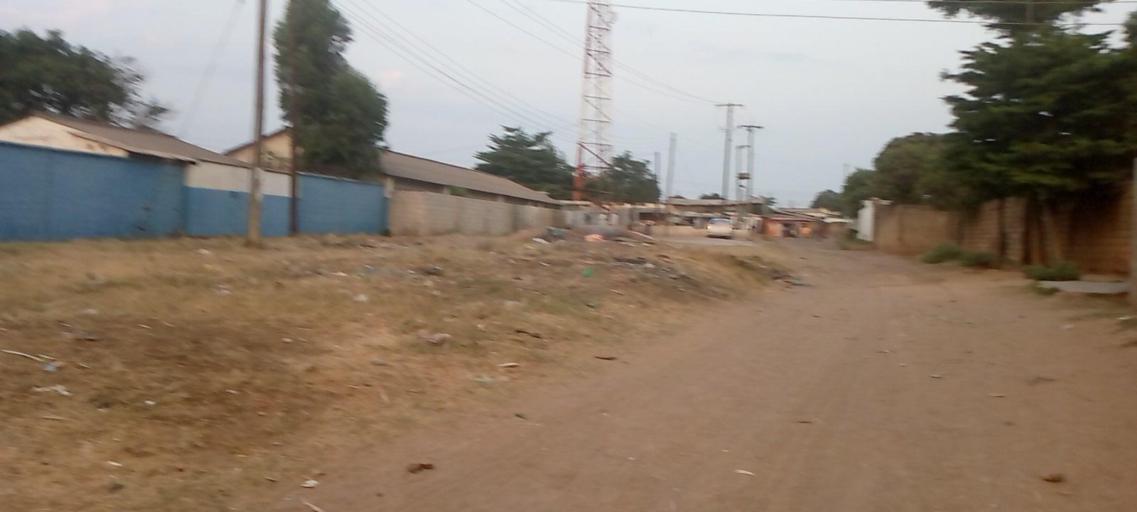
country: ZM
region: Lusaka
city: Lusaka
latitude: -15.4045
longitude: 28.3487
